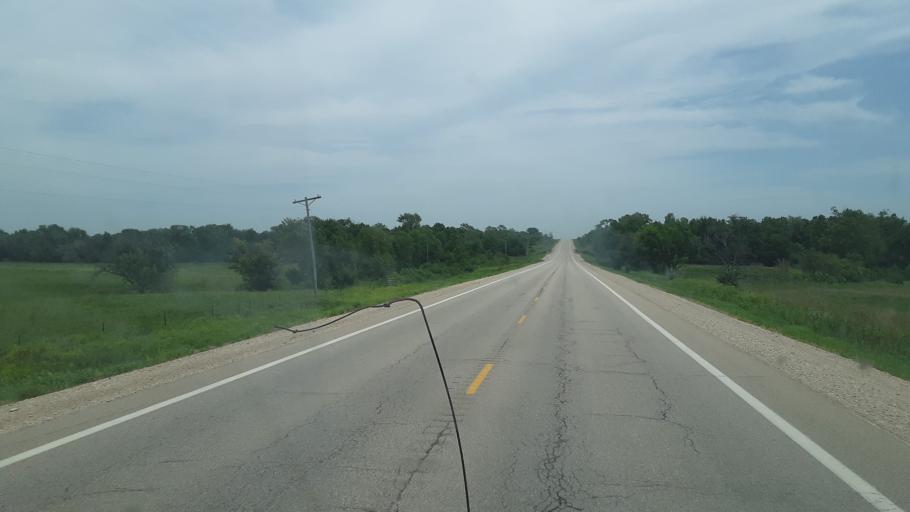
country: US
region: Kansas
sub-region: Woodson County
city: Yates Center
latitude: 37.8363
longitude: -95.9336
